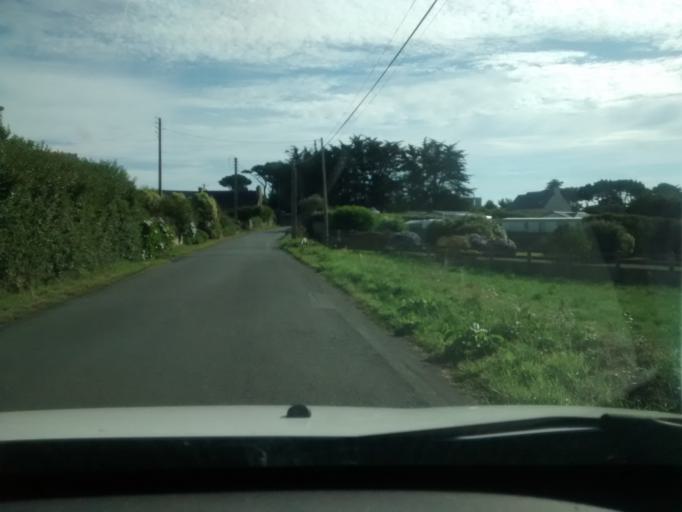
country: FR
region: Brittany
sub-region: Departement des Cotes-d'Armor
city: Plougrescant
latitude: 48.8588
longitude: -3.2206
